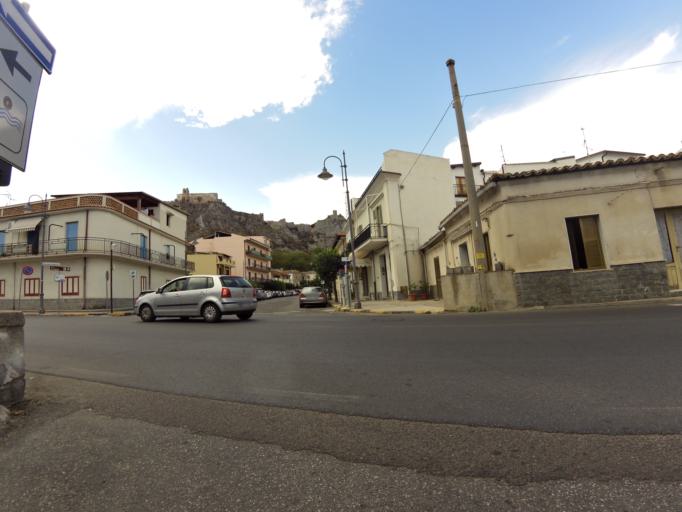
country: IT
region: Calabria
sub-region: Provincia di Reggio Calabria
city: Roccella Ionica
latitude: 38.3237
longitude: 16.4107
